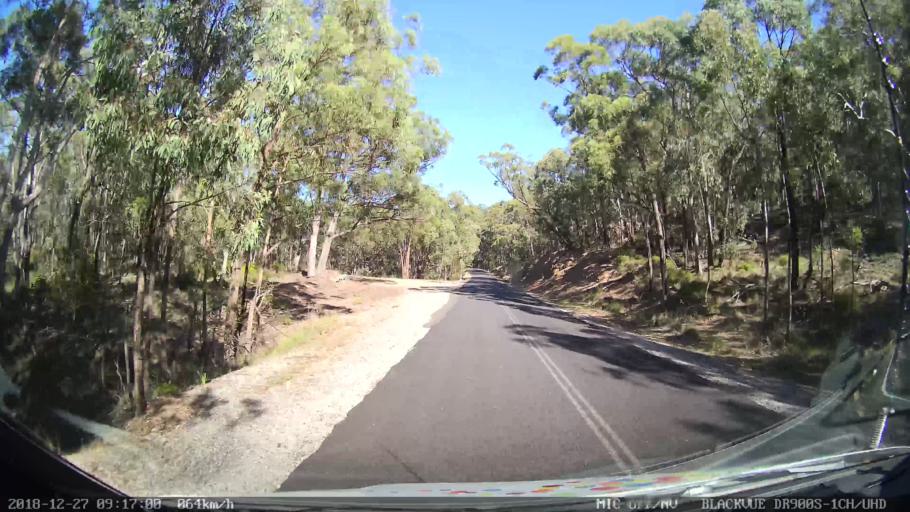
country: AU
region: New South Wales
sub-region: Lithgow
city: Portland
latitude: -33.1366
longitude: 150.0557
